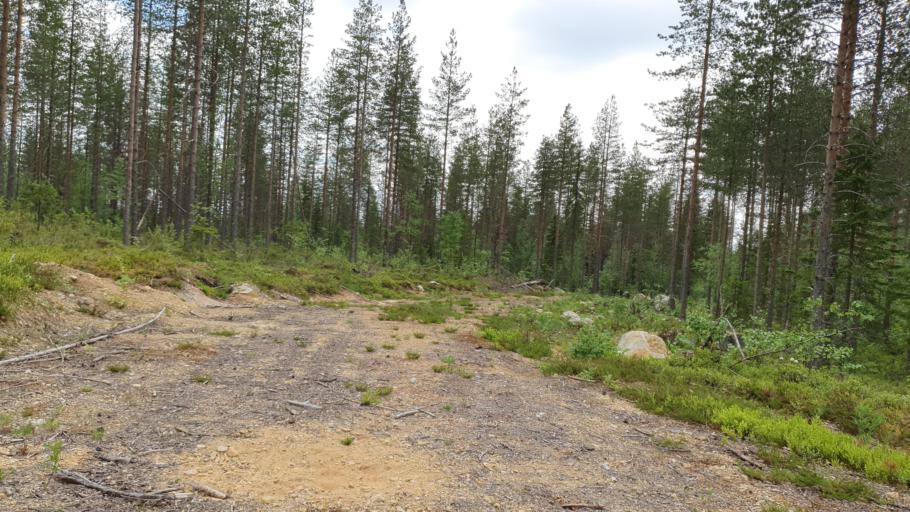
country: FI
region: Kainuu
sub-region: Kehys-Kainuu
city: Kuhmo
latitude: 64.4464
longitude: 29.6847
